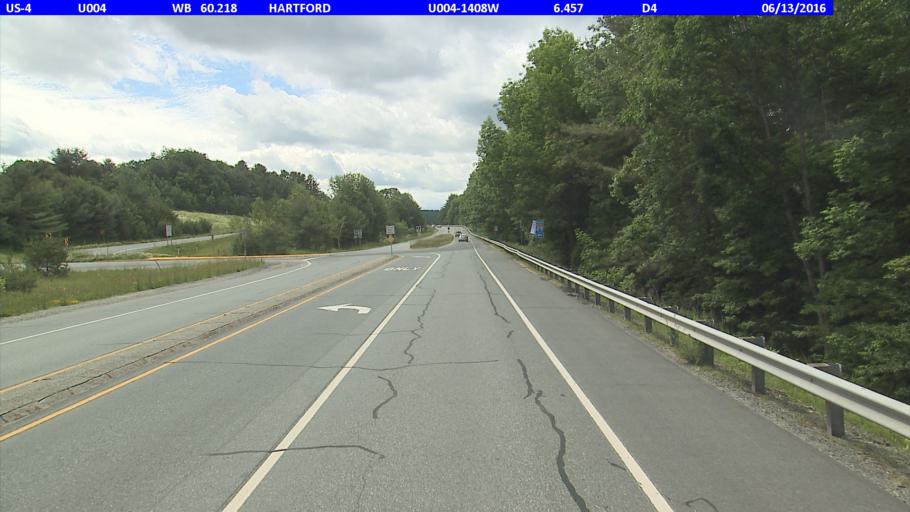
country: US
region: Vermont
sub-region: Windsor County
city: White River Junction
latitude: 43.6654
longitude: -72.3807
